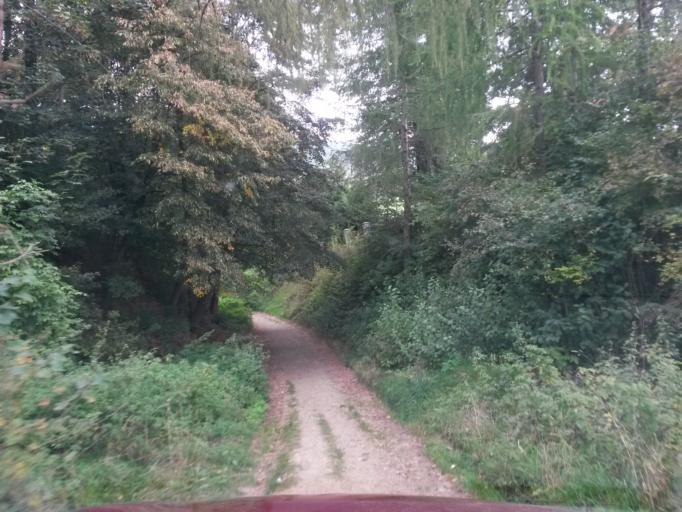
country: SK
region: Kosicky
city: Spisska Nova Ves
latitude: 48.8411
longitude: 20.6146
